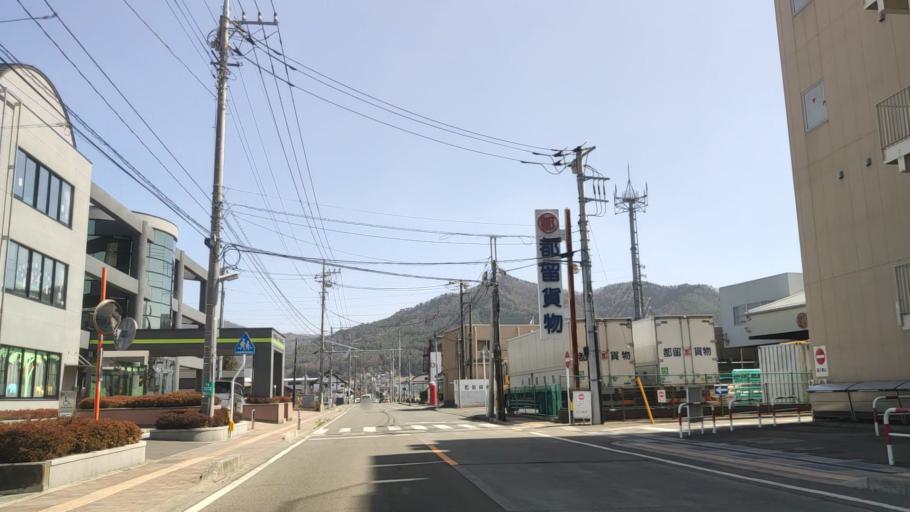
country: JP
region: Yamanashi
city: Fujikawaguchiko
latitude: 35.4875
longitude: 138.8083
